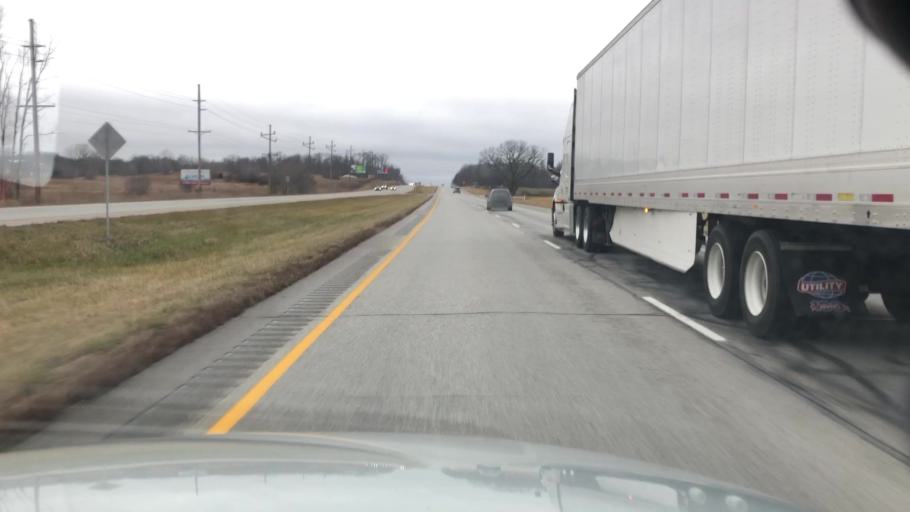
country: US
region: Indiana
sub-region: Kosciusko County
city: Pierceton
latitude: 41.2063
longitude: -85.7122
